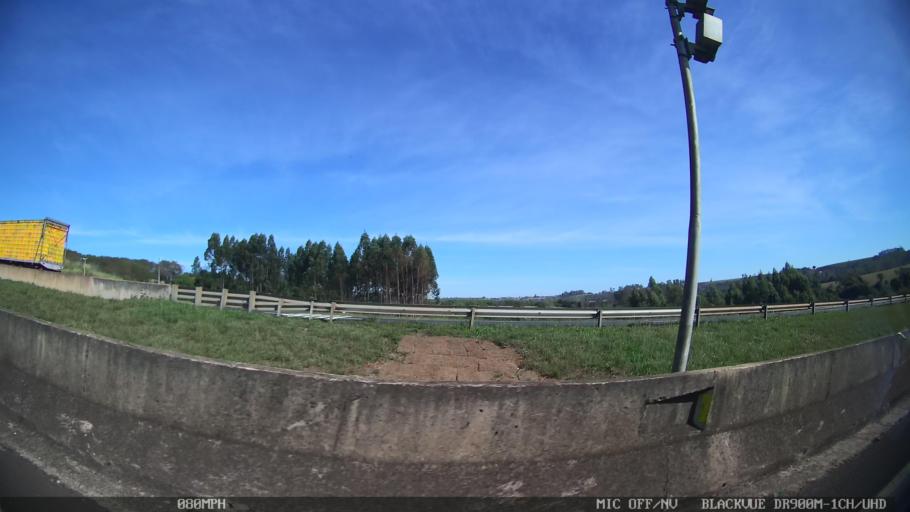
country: BR
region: Sao Paulo
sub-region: Leme
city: Leme
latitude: -22.1013
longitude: -47.4151
